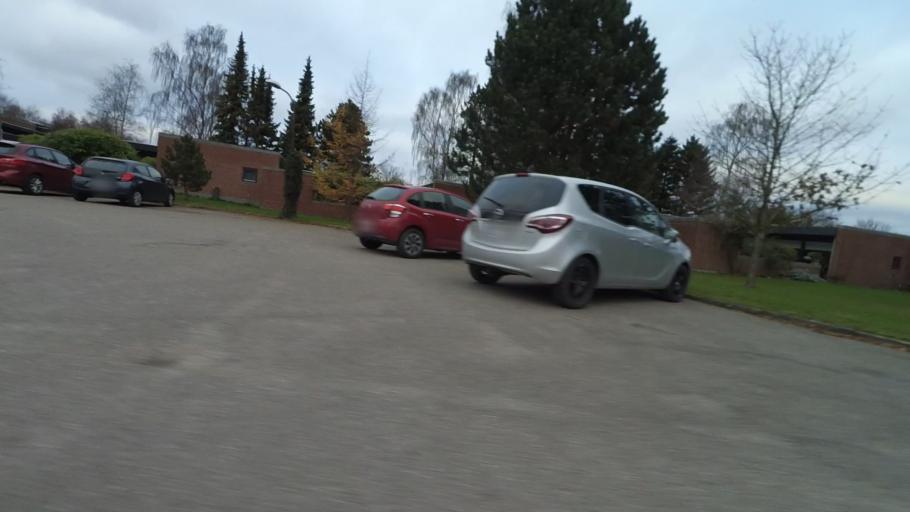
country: DK
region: Central Jutland
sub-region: Arhus Kommune
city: Stavtrup
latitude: 56.1596
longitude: 10.1166
